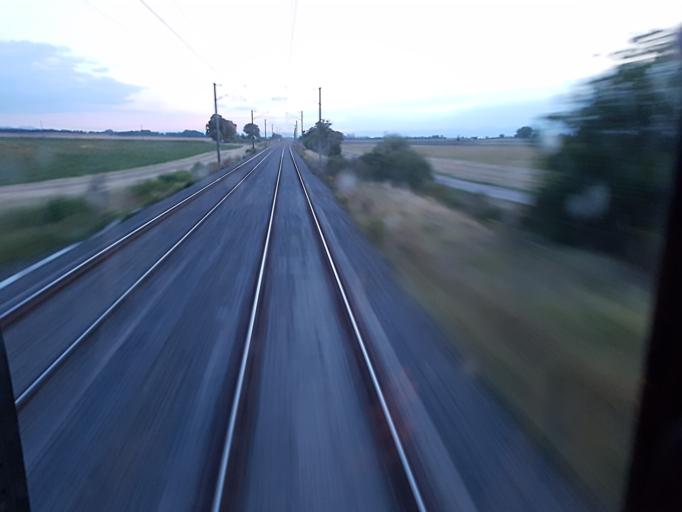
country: FR
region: Auvergne
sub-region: Departement du Puy-de-Dome
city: Ennezat
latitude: 45.9439
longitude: 3.2422
